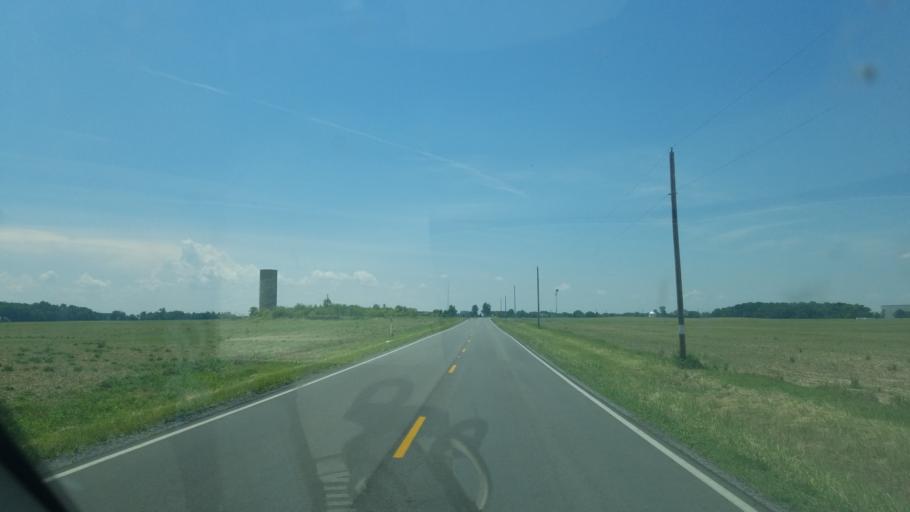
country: US
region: Ohio
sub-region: Hancock County
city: Findlay
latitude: 41.0866
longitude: -83.6153
